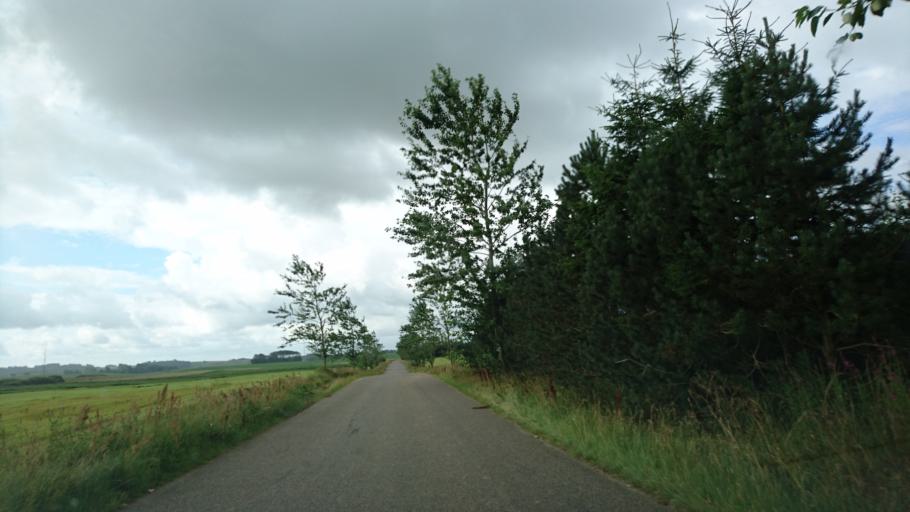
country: DK
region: North Denmark
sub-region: Hjorring Kommune
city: Sindal
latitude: 57.3757
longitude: 10.2130
